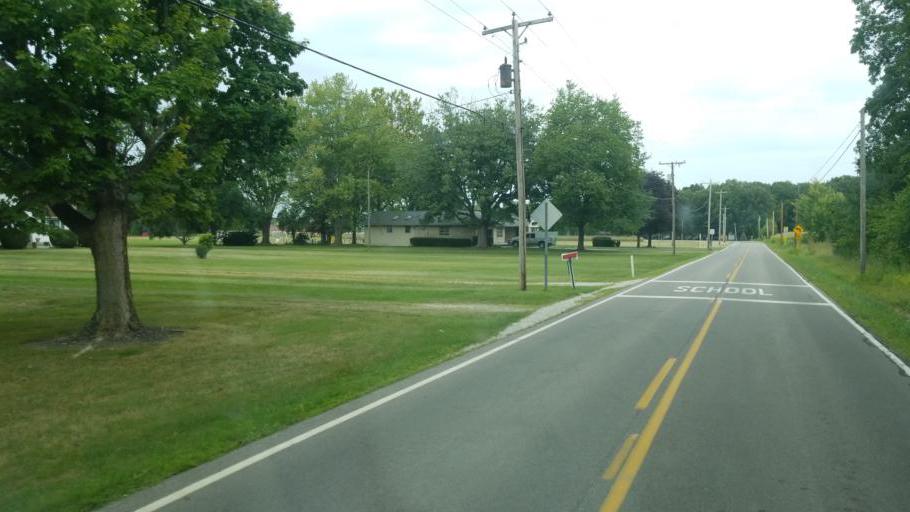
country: US
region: Ohio
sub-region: Marion County
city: Marion
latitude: 40.5140
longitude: -83.1313
